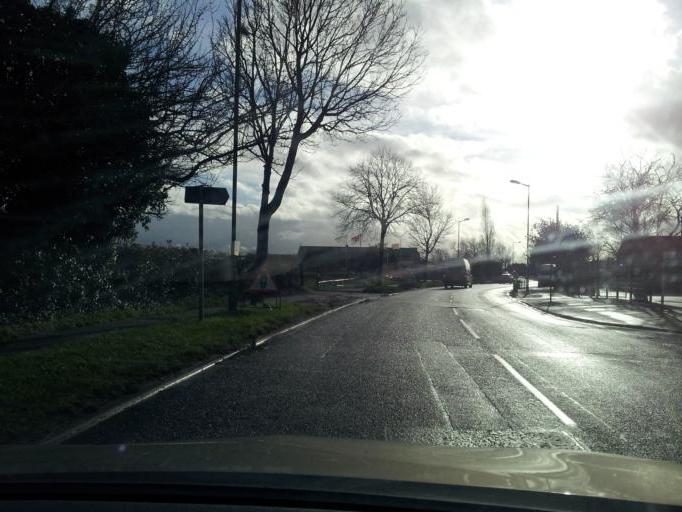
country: GB
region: England
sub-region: Nottinghamshire
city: Newark on Trent
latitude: 53.0631
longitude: -0.8039
